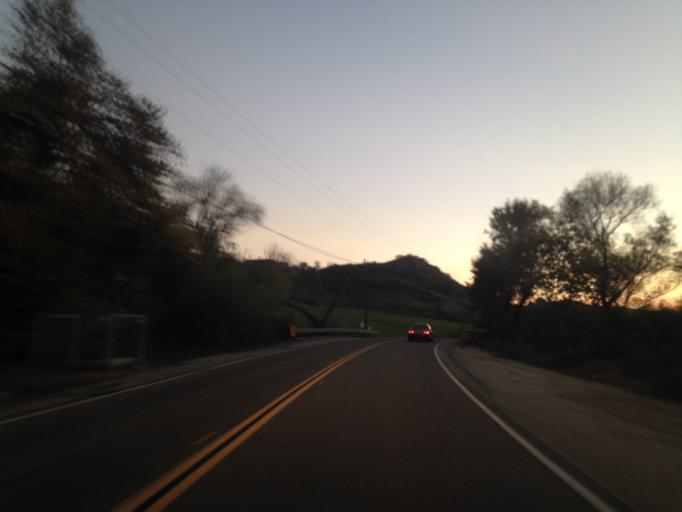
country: US
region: California
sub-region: San Diego County
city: Bonsall
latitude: 33.2664
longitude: -117.2331
